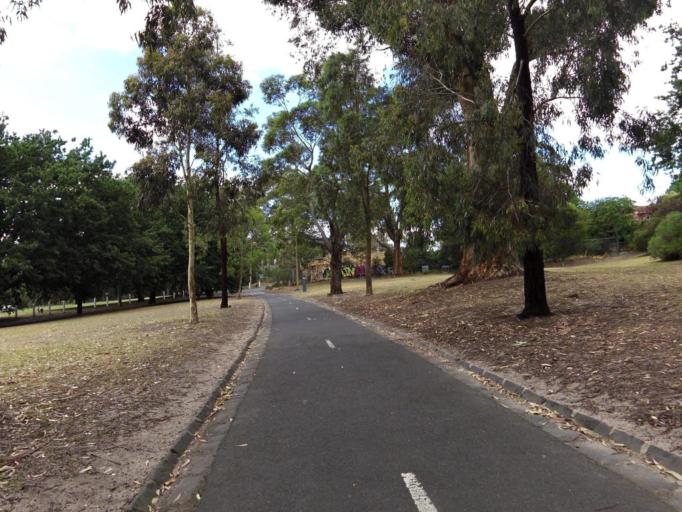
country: AU
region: Victoria
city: Balwyn
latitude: -37.8240
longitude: 145.0686
